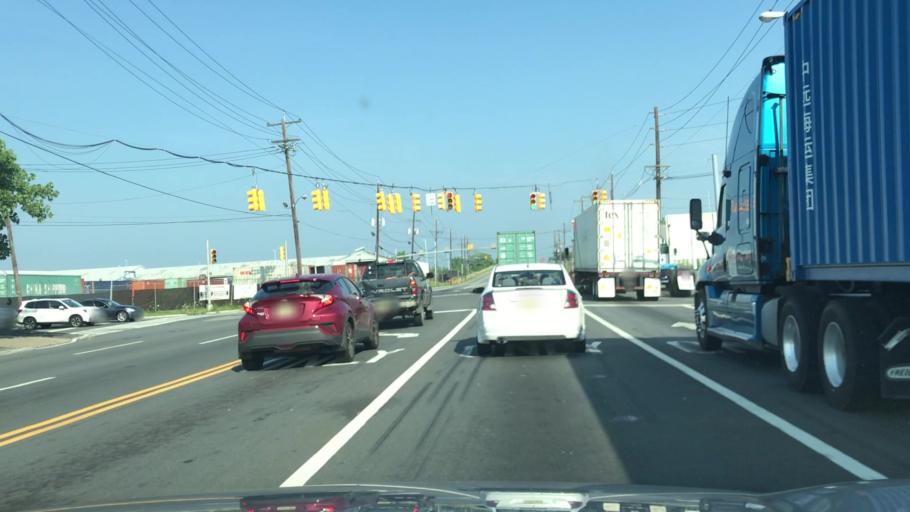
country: US
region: New Jersey
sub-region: Union County
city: Elizabeth
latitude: 40.6670
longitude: -74.1711
